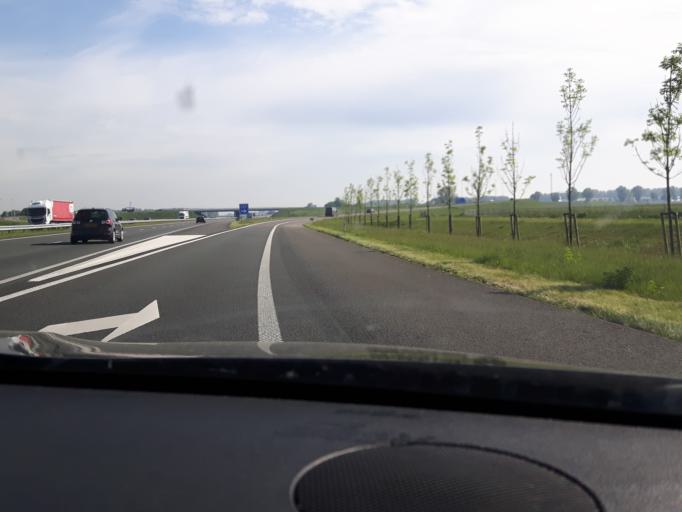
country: NL
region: North Brabant
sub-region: Gemeente Steenbergen
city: Steenbergen
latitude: 51.5857
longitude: 4.2908
